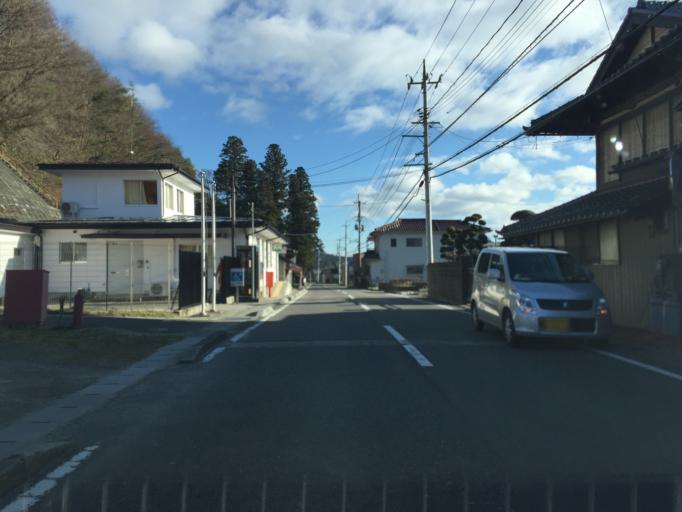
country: JP
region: Fukushima
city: Funehikimachi-funehiki
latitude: 37.2568
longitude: 140.6579
